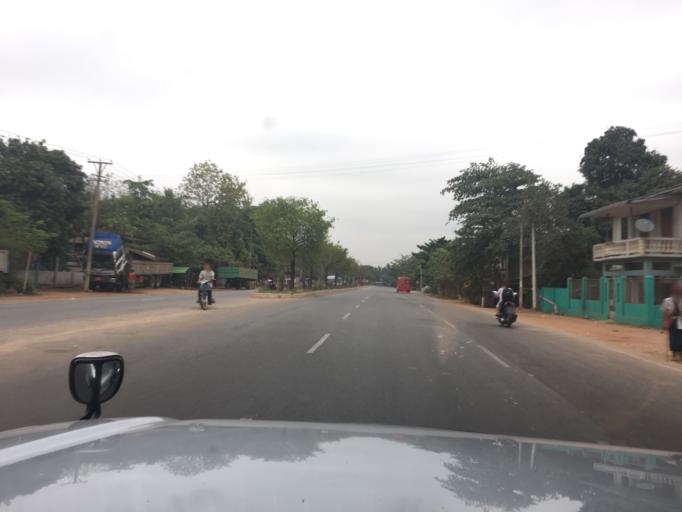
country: MM
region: Bago
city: Thanatpin
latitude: 17.1820
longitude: 96.3802
